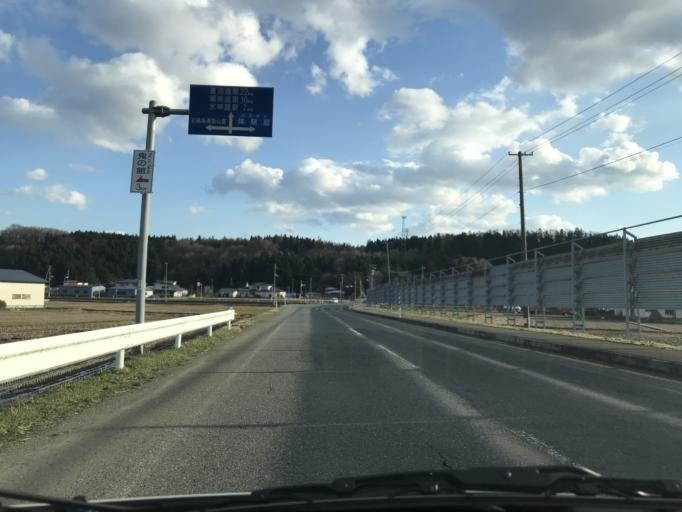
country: JP
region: Iwate
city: Kitakami
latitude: 39.2853
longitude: 141.0322
